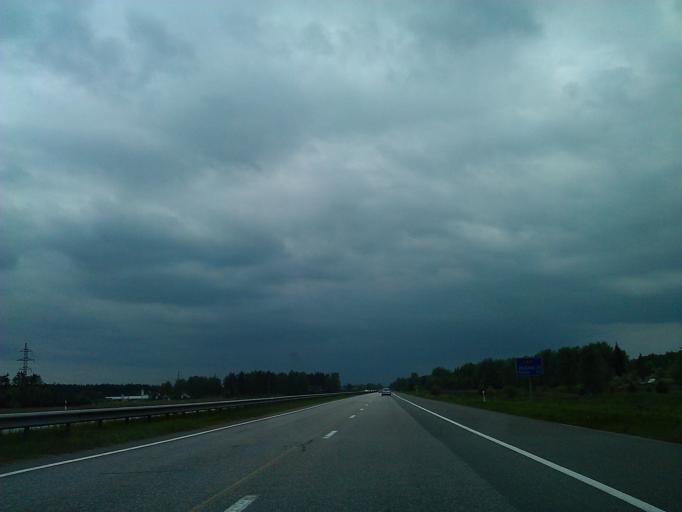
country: LV
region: Olaine
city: Olaine
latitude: 56.8149
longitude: 24.0089
